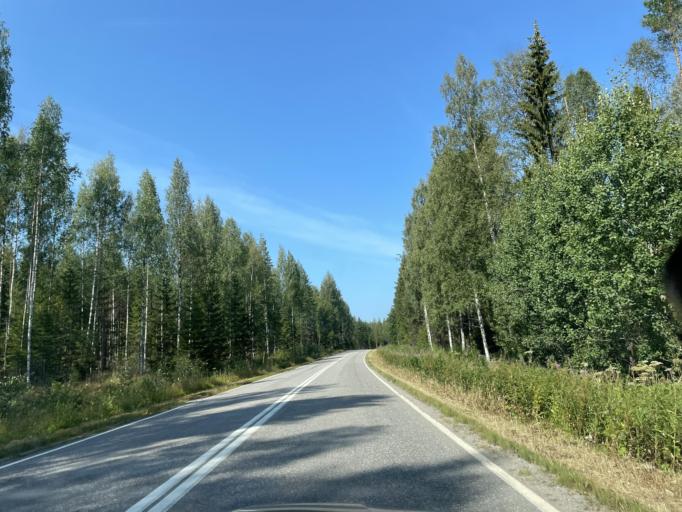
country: FI
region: Central Finland
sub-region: Saarijaervi-Viitasaari
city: Pihtipudas
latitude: 63.3655
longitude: 25.6973
